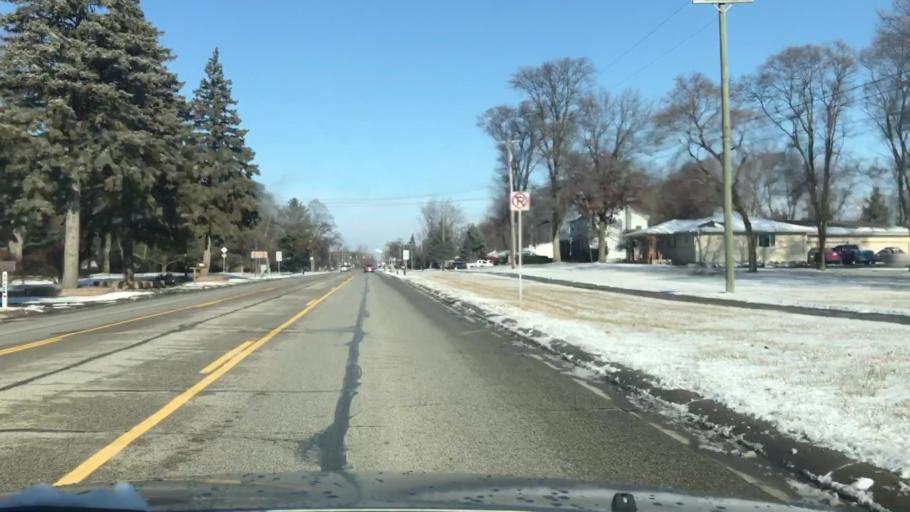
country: US
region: Michigan
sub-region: Oakland County
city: Rochester Hills
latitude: 42.6320
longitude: -83.1114
